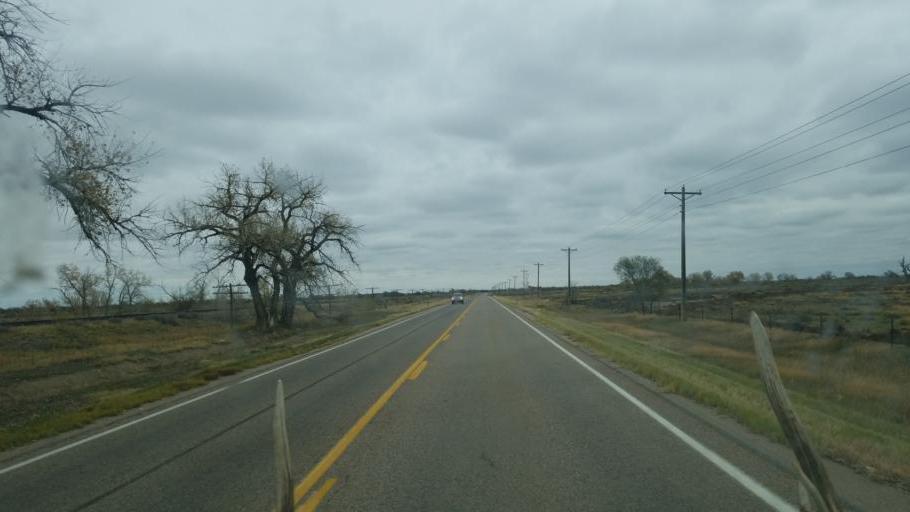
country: US
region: Colorado
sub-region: Crowley County
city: Ordway
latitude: 38.1977
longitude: -103.8370
